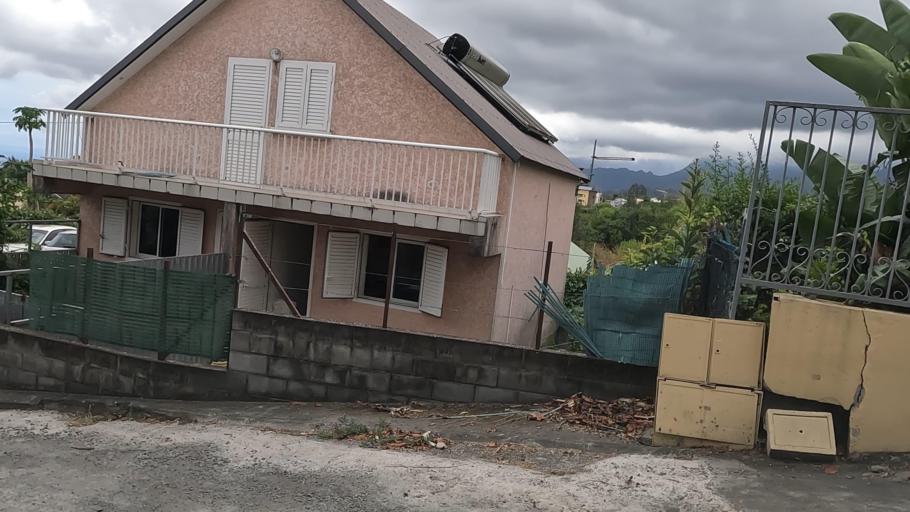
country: RE
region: Reunion
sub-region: Reunion
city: Le Tampon
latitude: -21.2670
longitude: 55.5117
